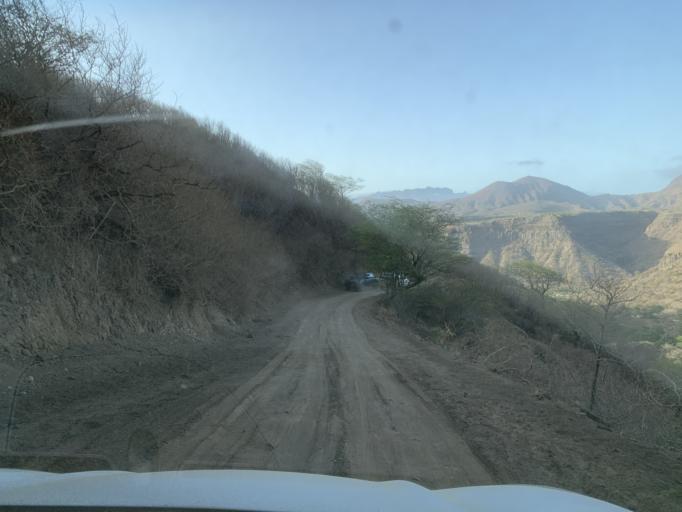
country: CV
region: Santa Catarina
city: Assomada
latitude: 15.0831
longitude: -23.7091
